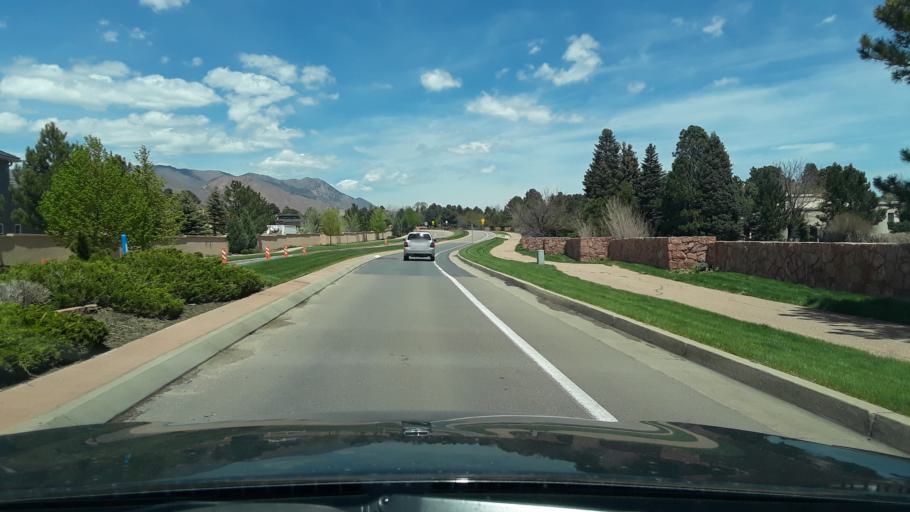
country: US
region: Colorado
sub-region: El Paso County
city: Manitou Springs
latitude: 38.8754
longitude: -104.8649
